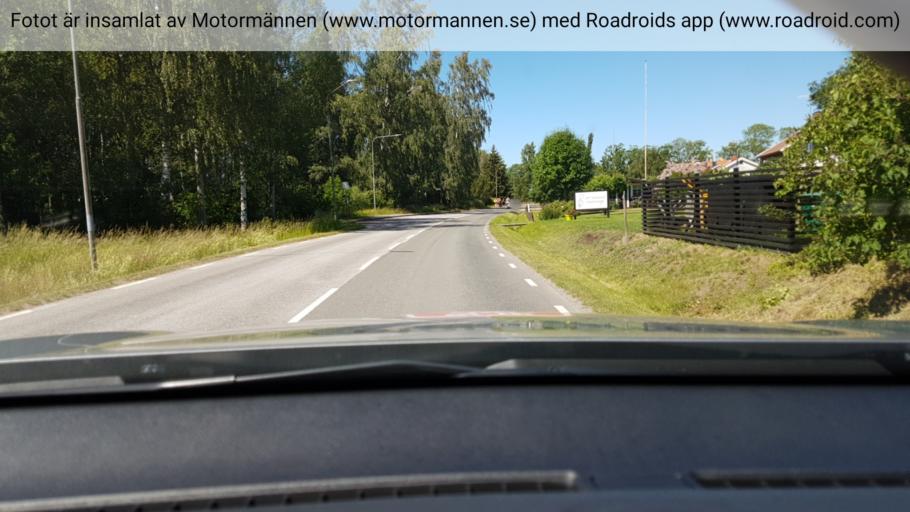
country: SE
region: Vaestra Goetaland
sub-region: Toreboda Kommun
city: Toereboda
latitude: 58.8320
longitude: 13.9830
